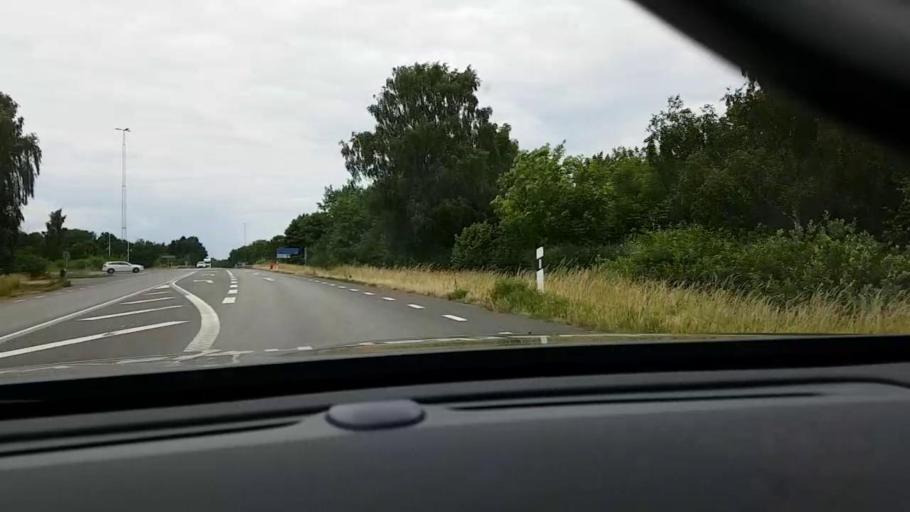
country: SE
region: Skane
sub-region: Hassleholms Kommun
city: Hassleholm
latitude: 56.1382
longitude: 13.8028
